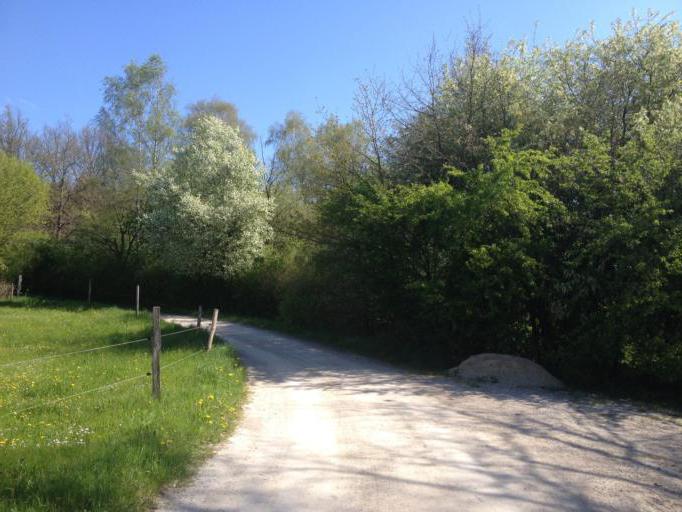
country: DE
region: Bavaria
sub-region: Regierungsbezirk Mittelfranken
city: Lauf an der Pegnitz
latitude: 49.5241
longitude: 11.2603
